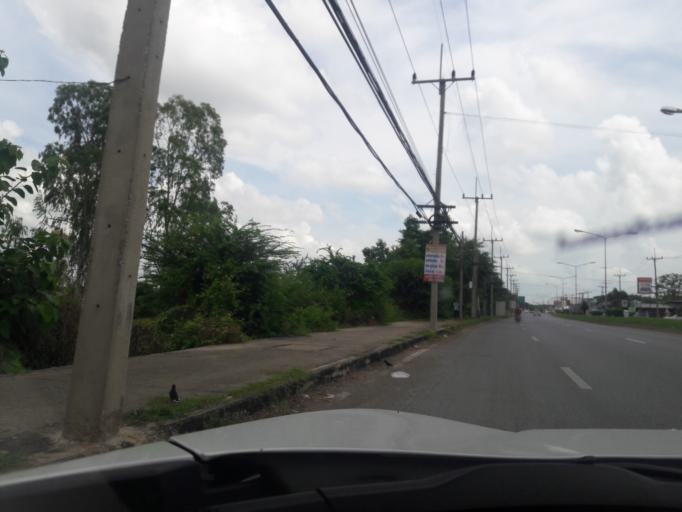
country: TH
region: Lop Buri
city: Ban Mi
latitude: 15.0454
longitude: 100.5521
